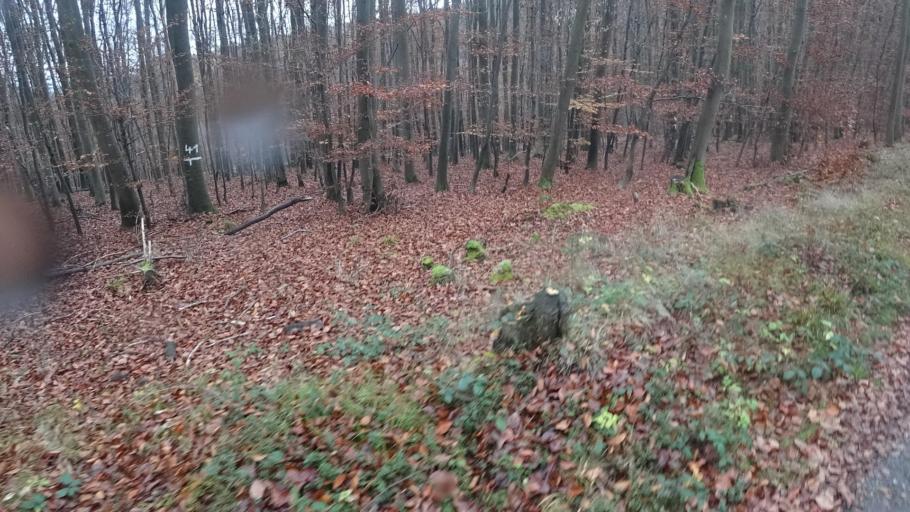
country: DE
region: Rheinland-Pfalz
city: Kestert
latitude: 50.1637
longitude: 7.6640
